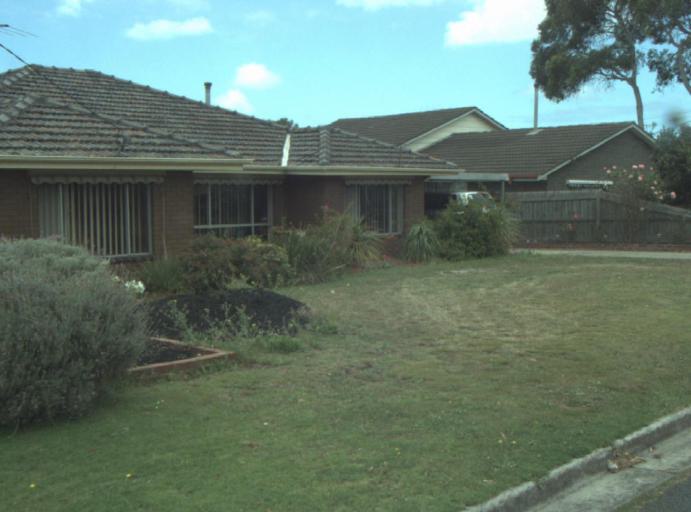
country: AU
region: Victoria
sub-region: Greater Geelong
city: Breakwater
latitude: -38.1869
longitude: 144.3410
